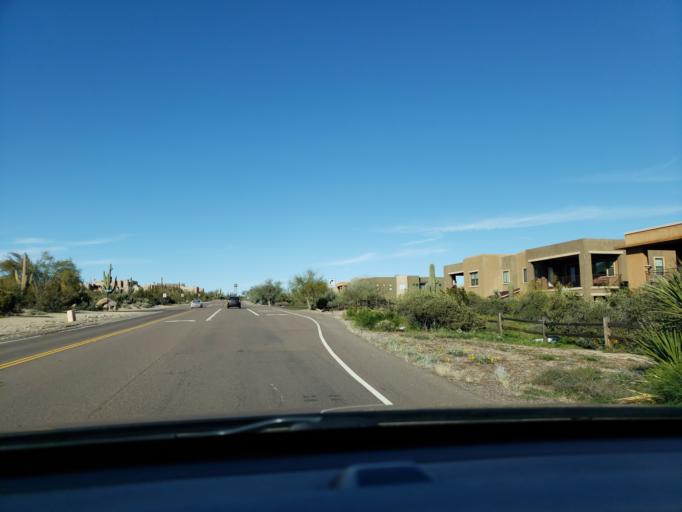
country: US
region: Arizona
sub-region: Maricopa County
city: Carefree
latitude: 33.7294
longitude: -111.8499
